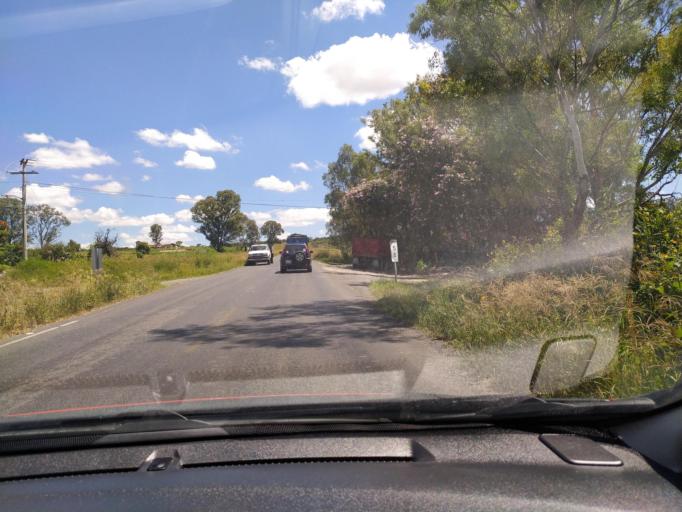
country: MX
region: Jalisco
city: San Diego de Alejandria
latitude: 21.0073
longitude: -102.0304
